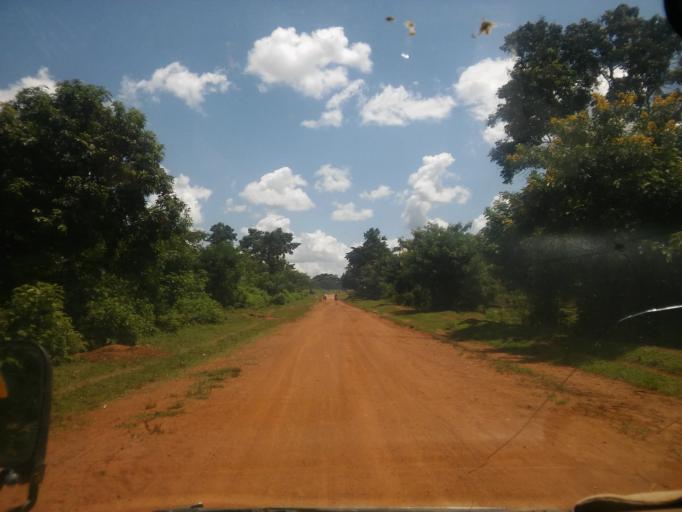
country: UG
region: Eastern Region
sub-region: Budaka District
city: Budaka
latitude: 1.1127
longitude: 33.9537
